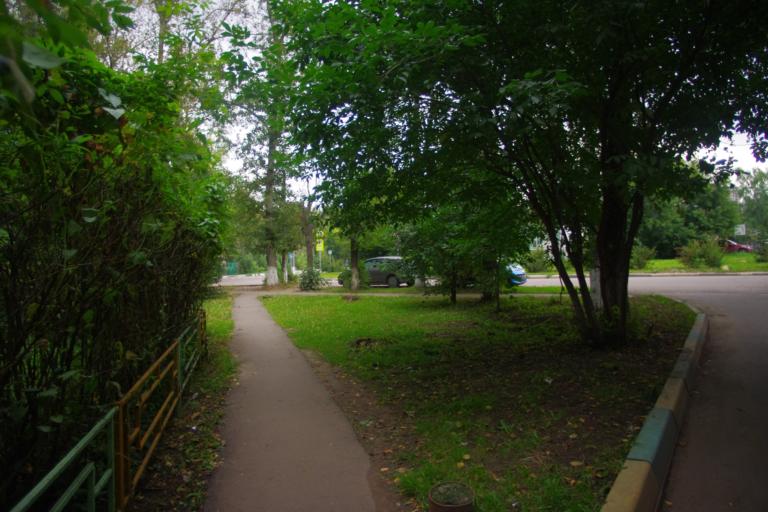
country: RU
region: Moskovskaya
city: Krasnogorsk
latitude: 55.8168
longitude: 37.3311
